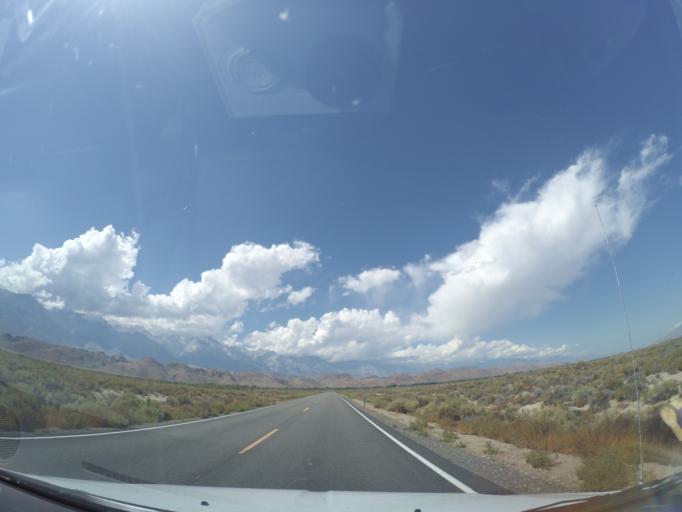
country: US
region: California
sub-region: Inyo County
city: Lone Pine
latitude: 36.5781
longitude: -118.0327
